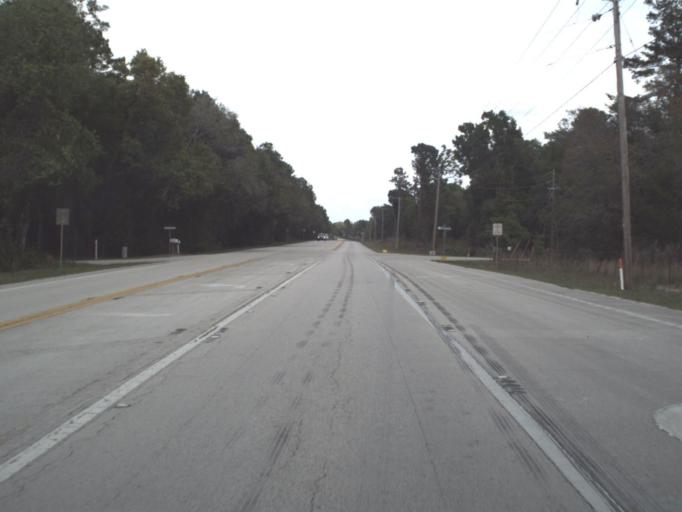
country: US
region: Florida
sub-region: Lake County
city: Mount Plymouth
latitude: 28.8903
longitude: -81.4640
